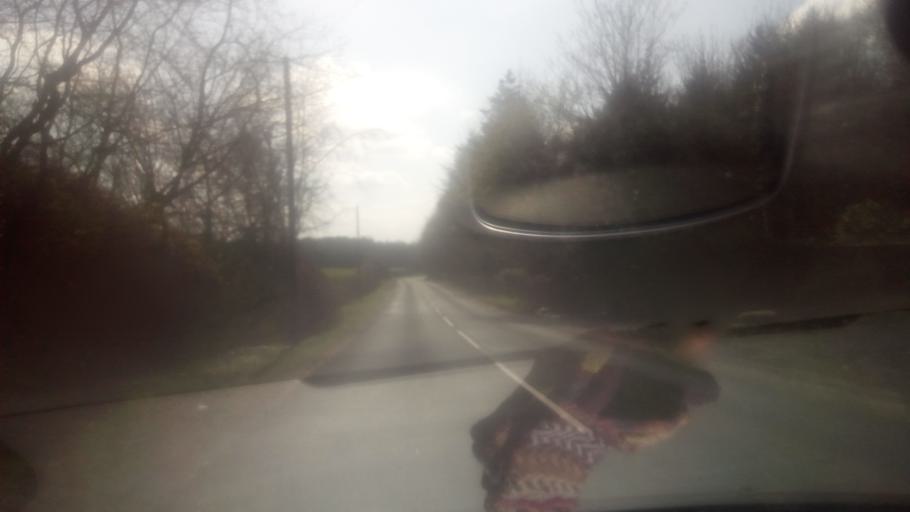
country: GB
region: Scotland
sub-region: The Scottish Borders
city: Kelso
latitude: 55.5498
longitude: -2.4620
